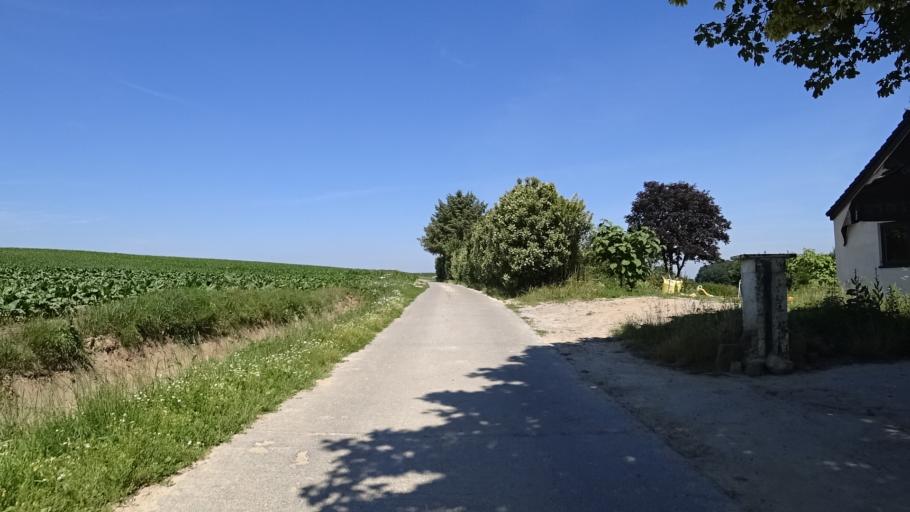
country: BE
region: Wallonia
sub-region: Province du Brabant Wallon
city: Perwez
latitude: 50.6541
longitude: 4.8462
